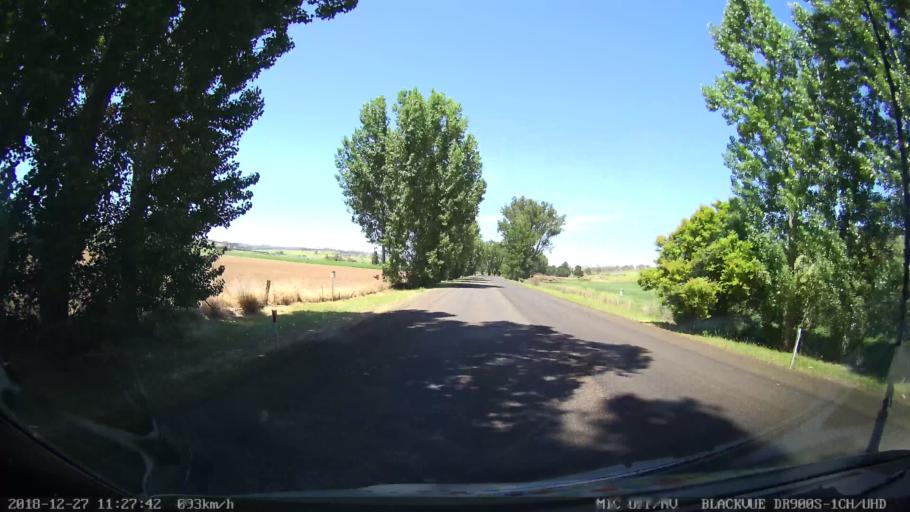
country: AU
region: New South Wales
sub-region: Bathurst Regional
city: Perthville
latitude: -33.4681
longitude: 149.5687
